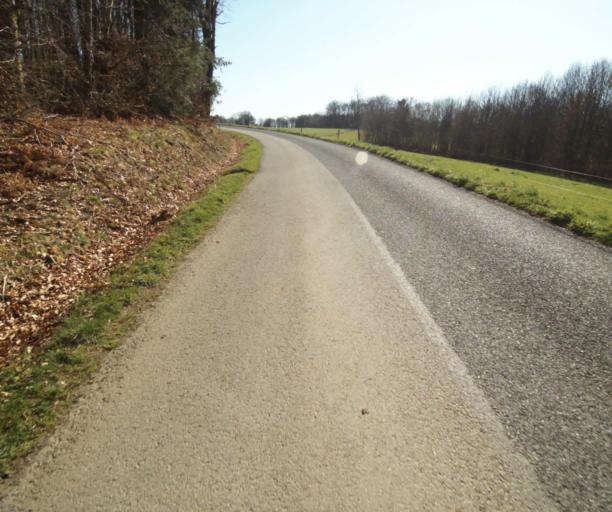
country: FR
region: Limousin
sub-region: Departement de la Correze
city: Chamboulive
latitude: 45.4807
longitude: 1.7116
